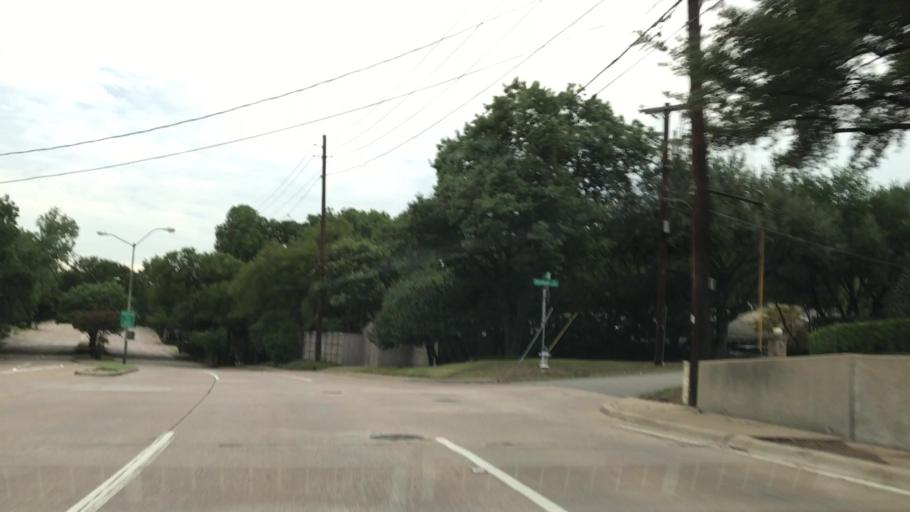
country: US
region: Texas
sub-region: Dallas County
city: University Park
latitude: 32.9064
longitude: -96.7864
